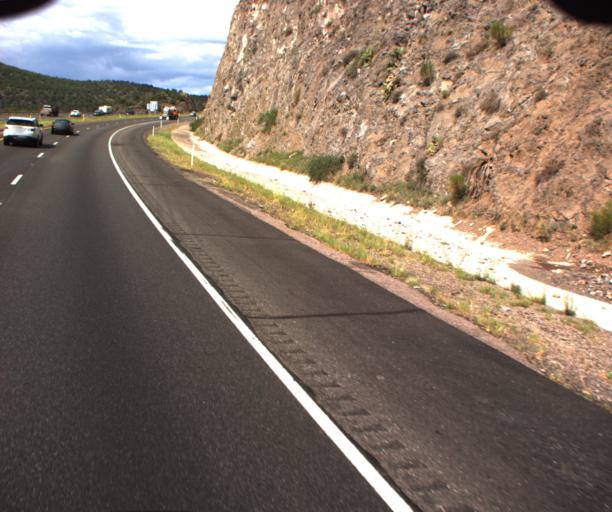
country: US
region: Arizona
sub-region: Yavapai County
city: Camp Verde
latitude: 34.5322
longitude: -111.9416
